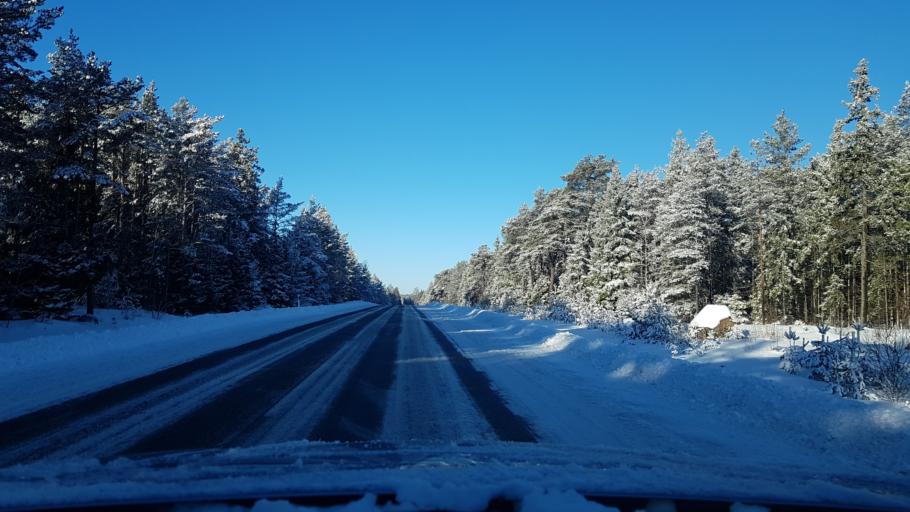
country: EE
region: Hiiumaa
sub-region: Kaerdla linn
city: Kardla
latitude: 58.9596
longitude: 22.8538
